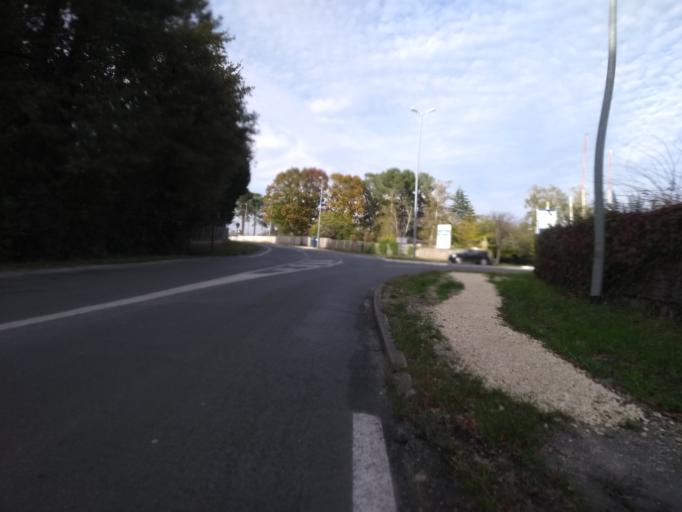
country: FR
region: Aquitaine
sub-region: Departement de la Gironde
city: Pessac
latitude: 44.7842
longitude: -0.6635
